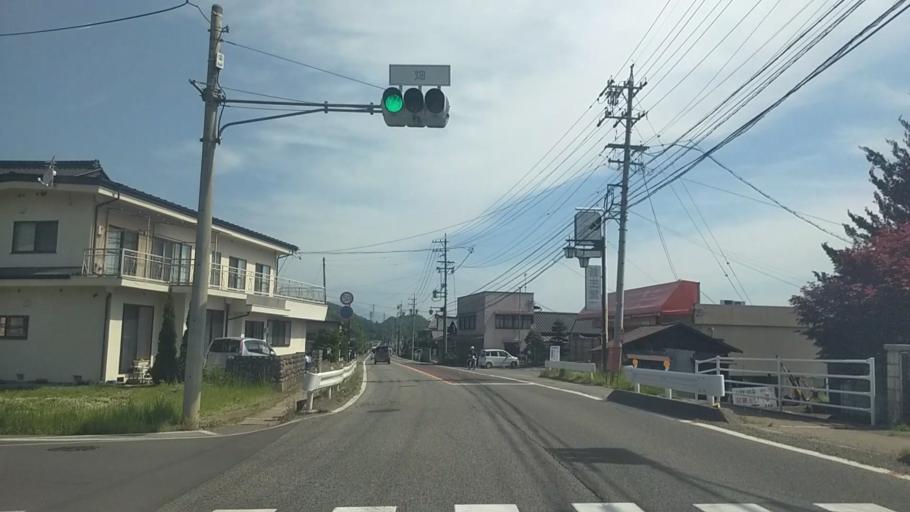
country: JP
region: Nagano
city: Saku
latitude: 36.1440
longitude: 138.4732
